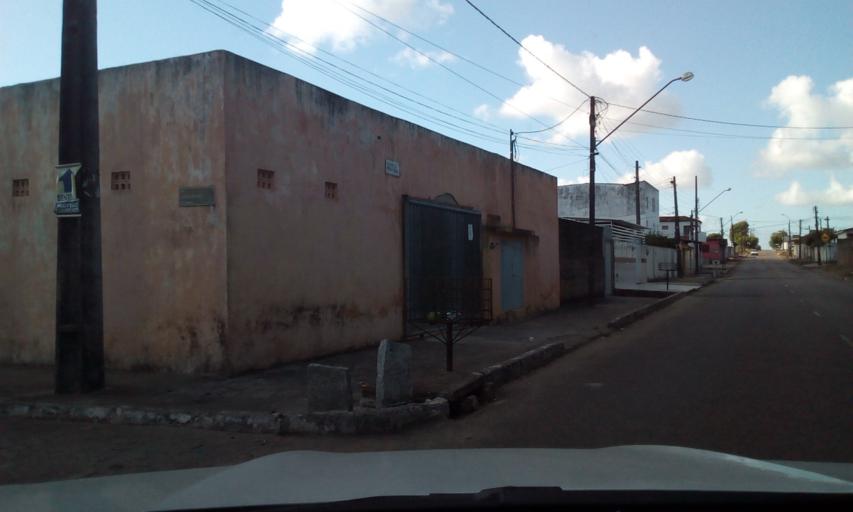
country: BR
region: Paraiba
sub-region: Bayeux
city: Bayeux
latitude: -7.1431
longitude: -34.9085
